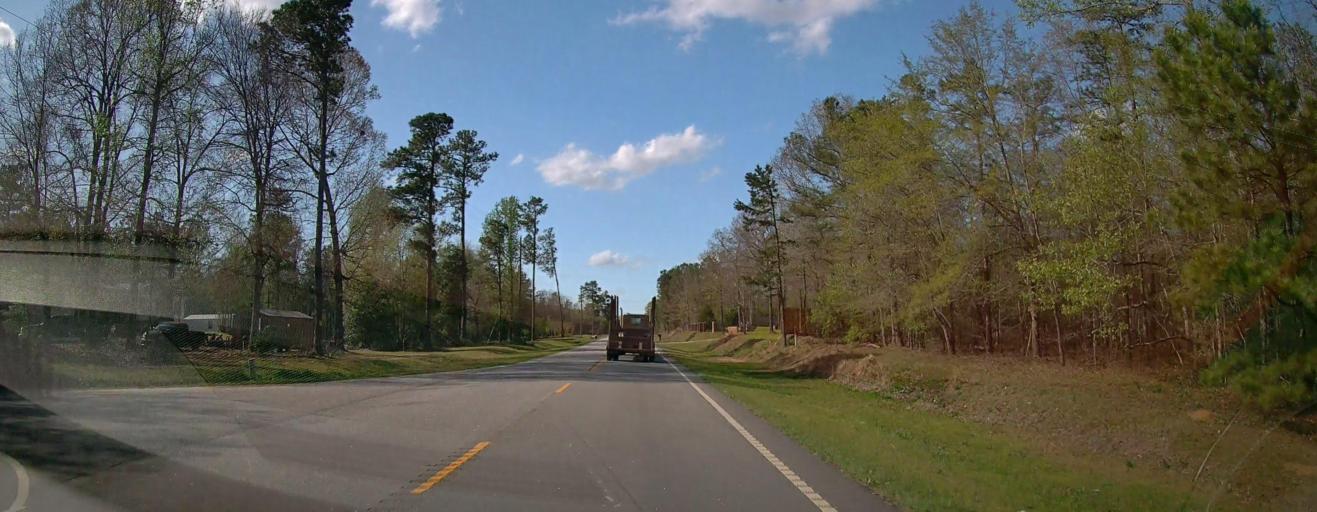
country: US
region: Georgia
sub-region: Baldwin County
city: Hardwick
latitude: 33.0623
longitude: -83.1314
